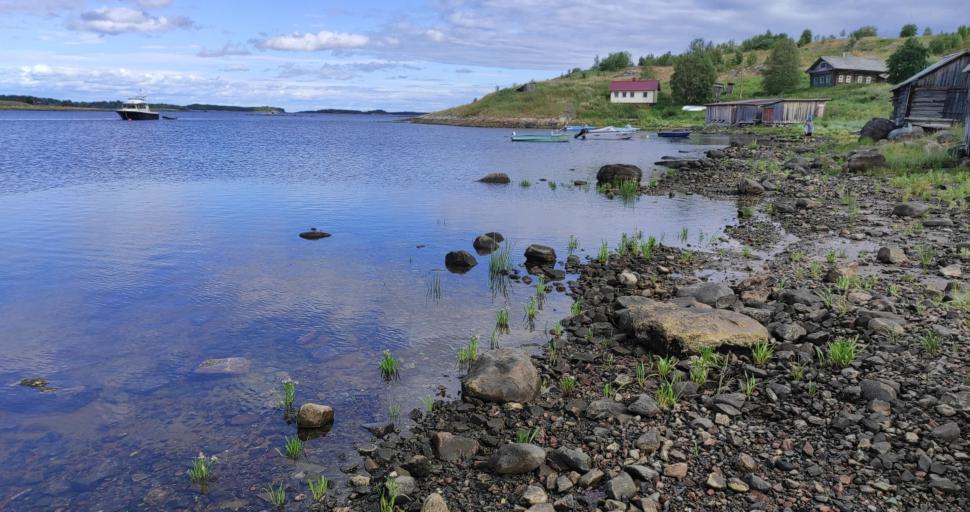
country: RU
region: Murmansk
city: Poyakonda
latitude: 66.6938
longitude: 32.8588
